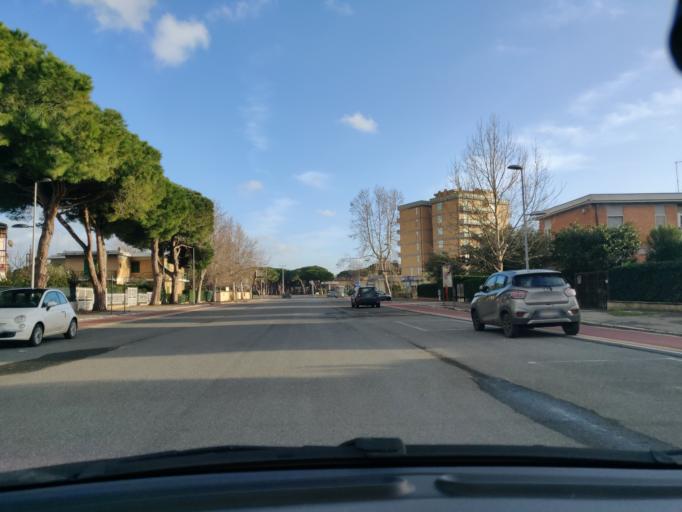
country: IT
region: Latium
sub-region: Provincia di Viterbo
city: Tarquinia
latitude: 42.2223
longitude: 11.7086
